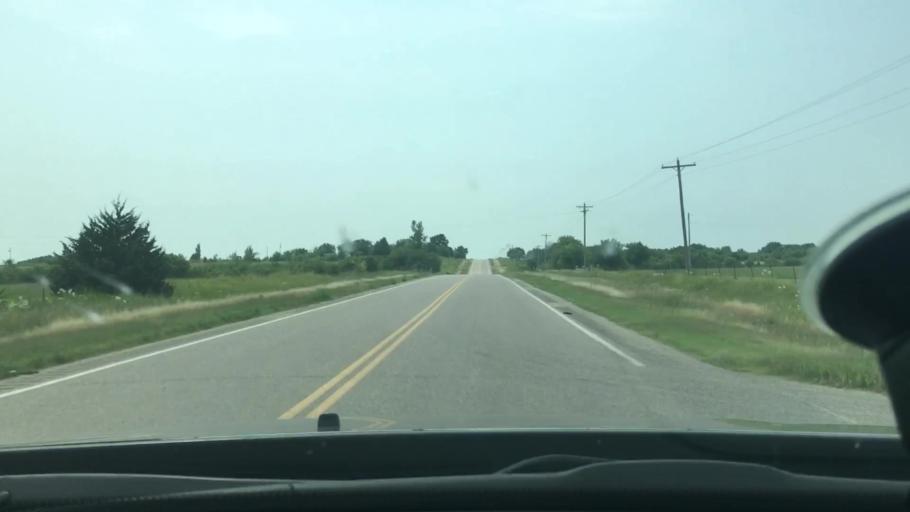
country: US
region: Oklahoma
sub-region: Marshall County
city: Madill
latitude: 34.0383
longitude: -96.7611
